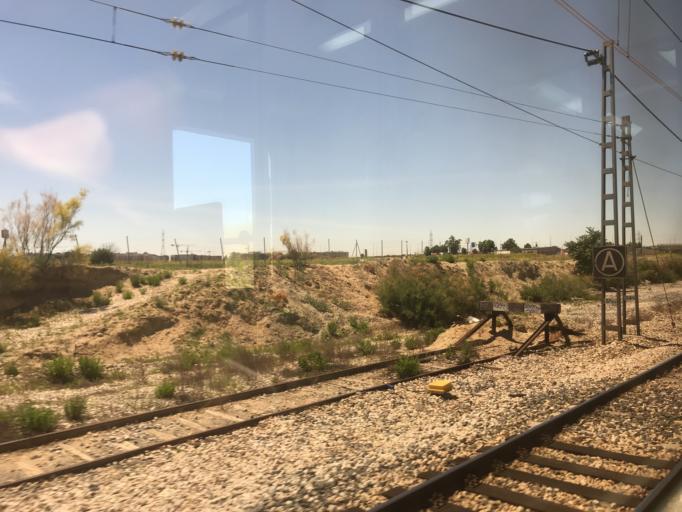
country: ES
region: Madrid
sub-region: Provincia de Madrid
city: Villaverde
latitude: 40.3303
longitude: -3.7031
